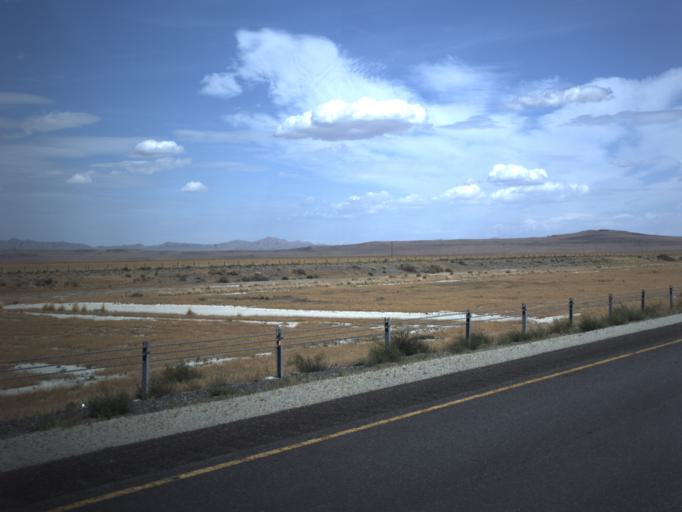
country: US
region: Utah
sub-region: Tooele County
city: Grantsville
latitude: 40.7261
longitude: -113.2256
